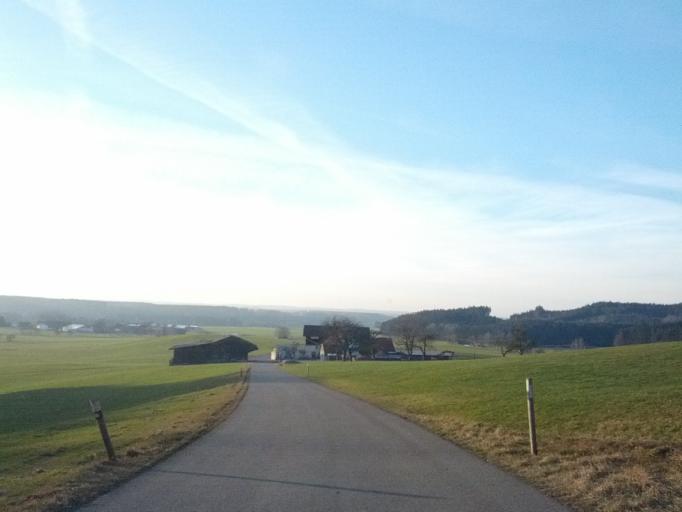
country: DE
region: Bavaria
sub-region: Swabia
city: Woringen
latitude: 47.8791
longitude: 10.1920
